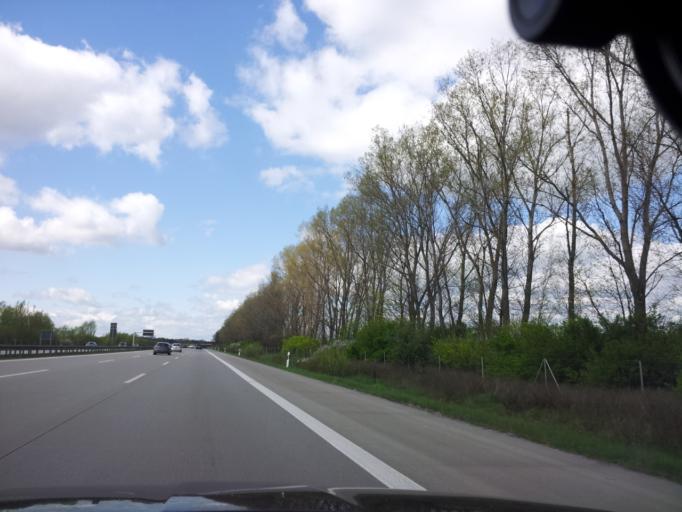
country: DE
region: Brandenburg
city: Neuenhagen
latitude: 52.5582
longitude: 13.6641
